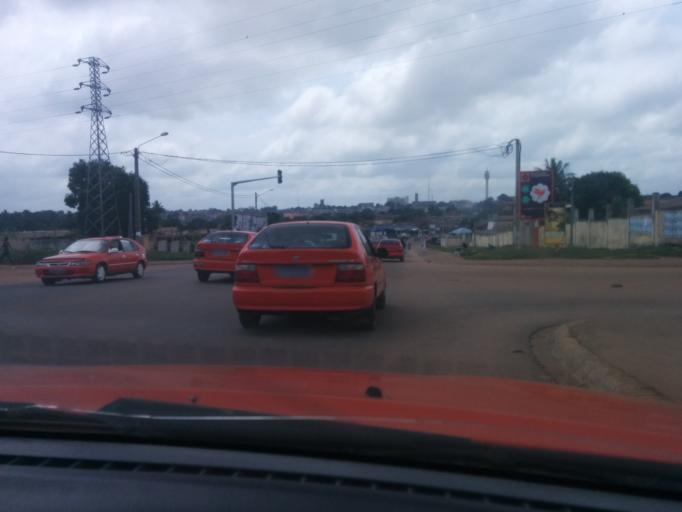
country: CI
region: Vallee du Bandama
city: Bouake
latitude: 7.6978
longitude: -5.0338
